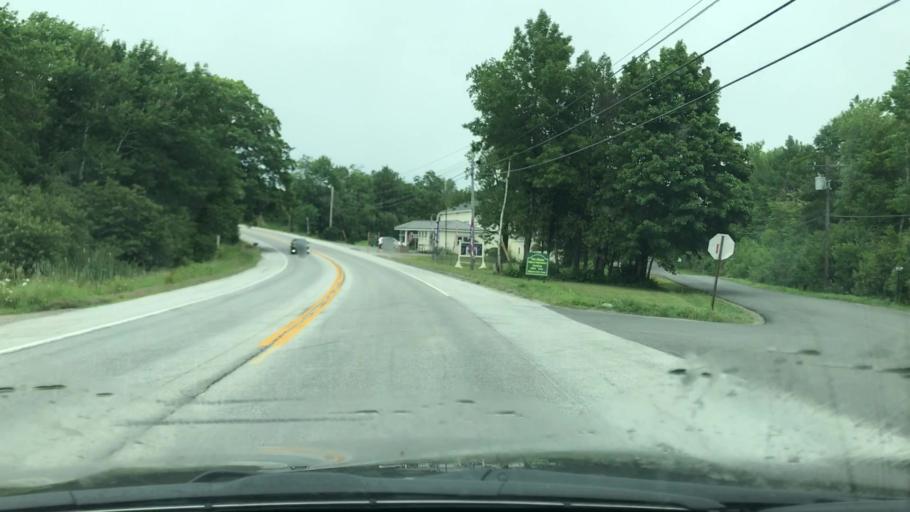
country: US
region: Maine
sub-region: Waldo County
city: Northport
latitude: 44.3330
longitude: -68.9570
